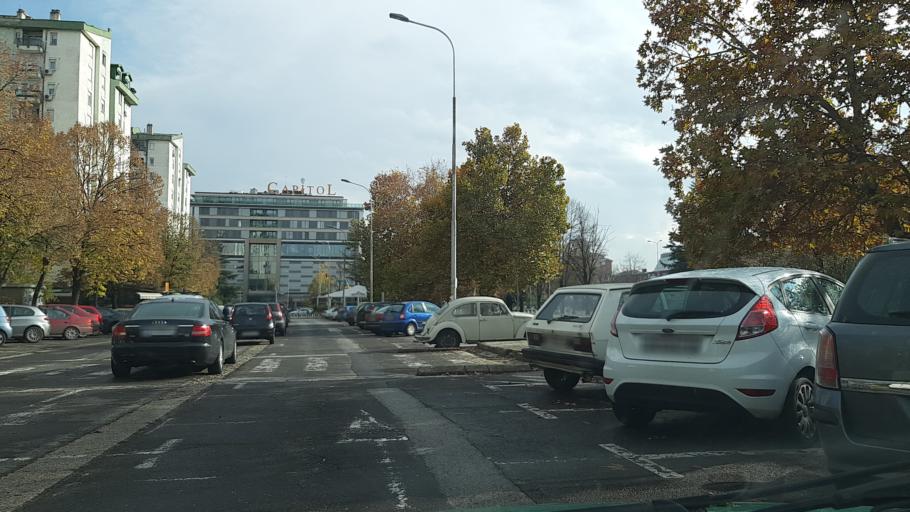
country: MK
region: Kisela Voda
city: Usje
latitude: 41.9871
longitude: 21.4643
